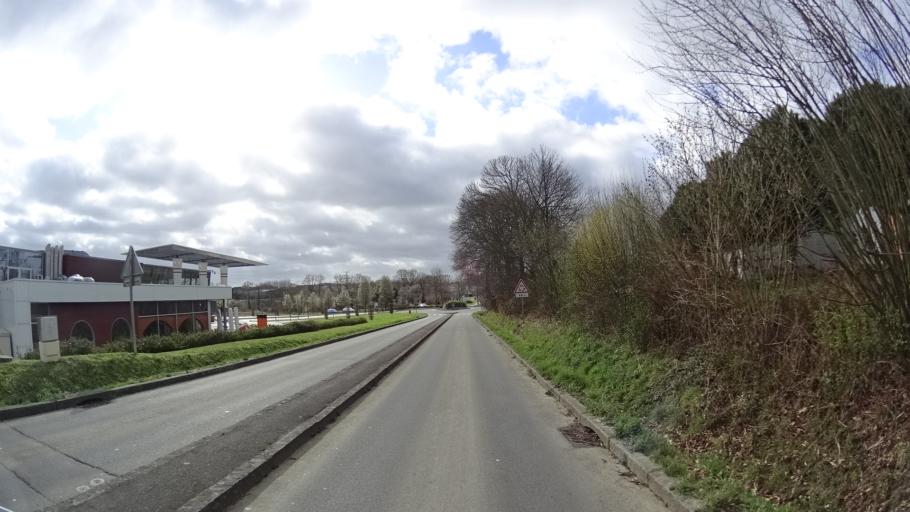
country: FR
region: Brittany
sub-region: Departement d'Ille-et-Vilaine
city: La Meziere
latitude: 48.2065
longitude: -1.7310
